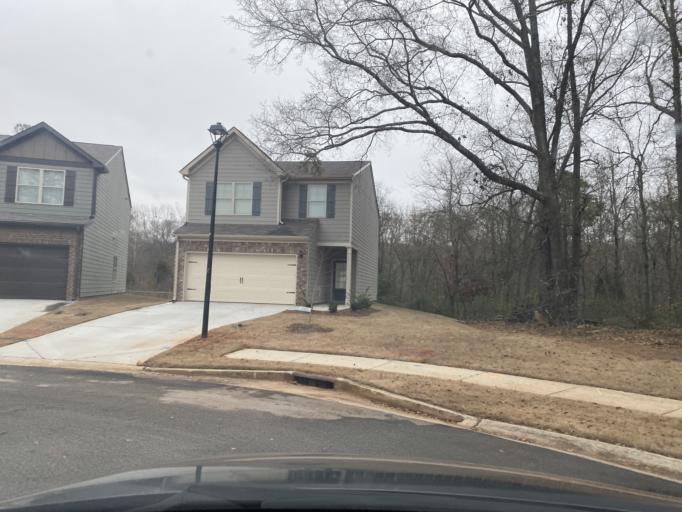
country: US
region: Georgia
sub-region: DeKalb County
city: Pine Mountain
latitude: 33.6879
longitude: -84.1527
